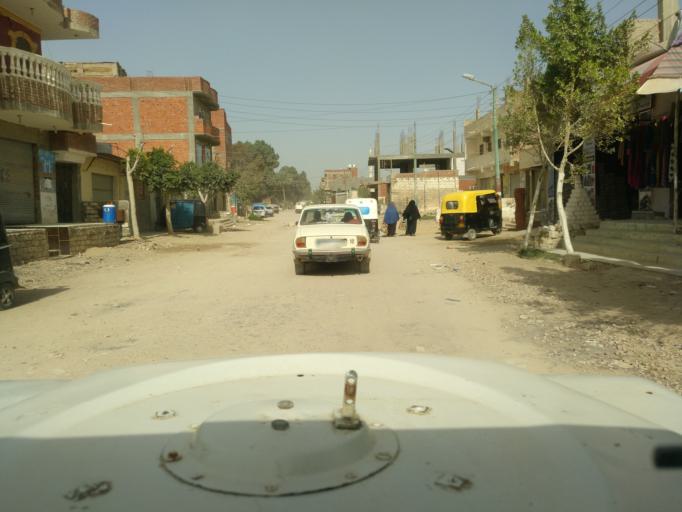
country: EG
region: Al Buhayrah
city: Beheira
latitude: 30.3705
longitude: 30.3558
